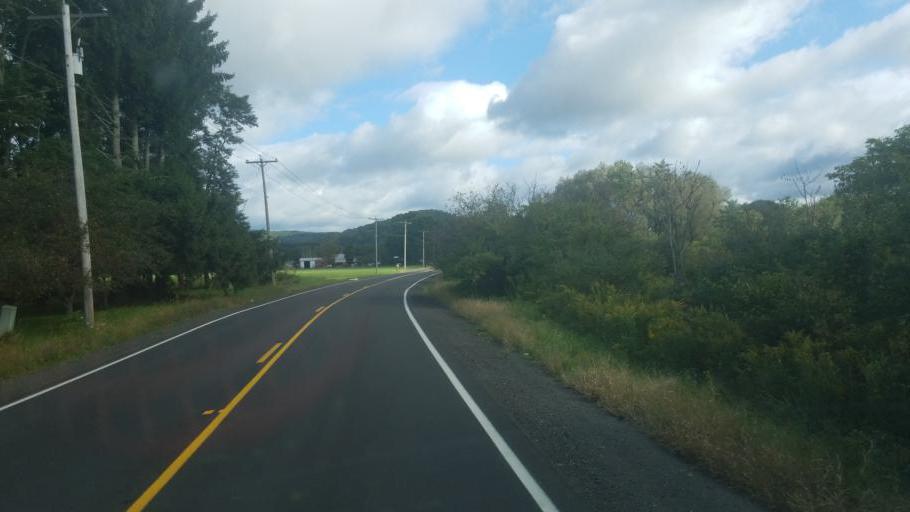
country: US
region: New York
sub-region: Cattaraugus County
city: Weston Mills
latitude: 42.0834
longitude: -78.3680
